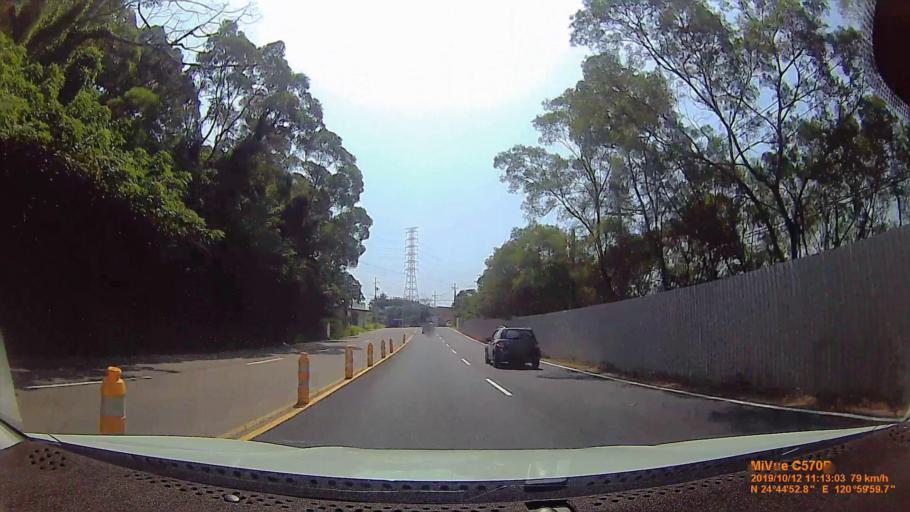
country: TW
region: Taiwan
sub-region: Hsinchu
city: Hsinchu
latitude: 24.7478
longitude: 121.0000
